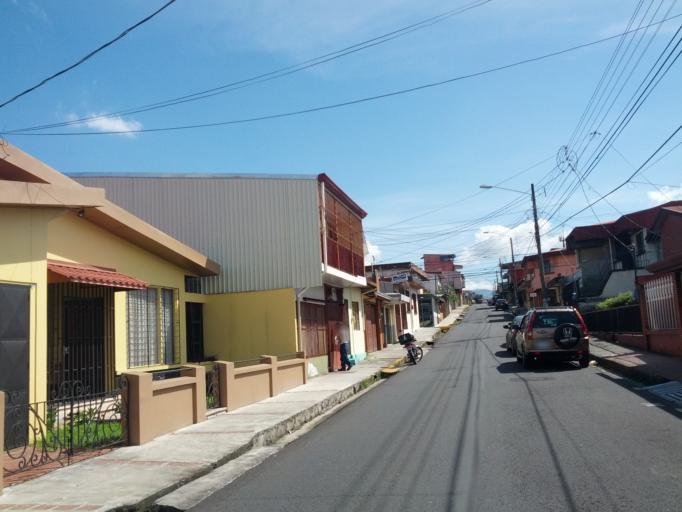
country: CR
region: Alajuela
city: Alajuela
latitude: 10.0161
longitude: -84.2103
